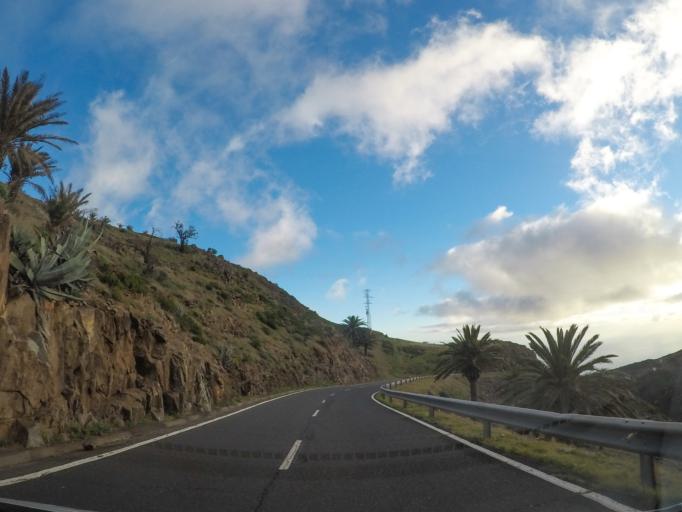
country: ES
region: Canary Islands
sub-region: Provincia de Santa Cruz de Tenerife
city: Alajero
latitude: 28.0844
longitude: -17.2452
